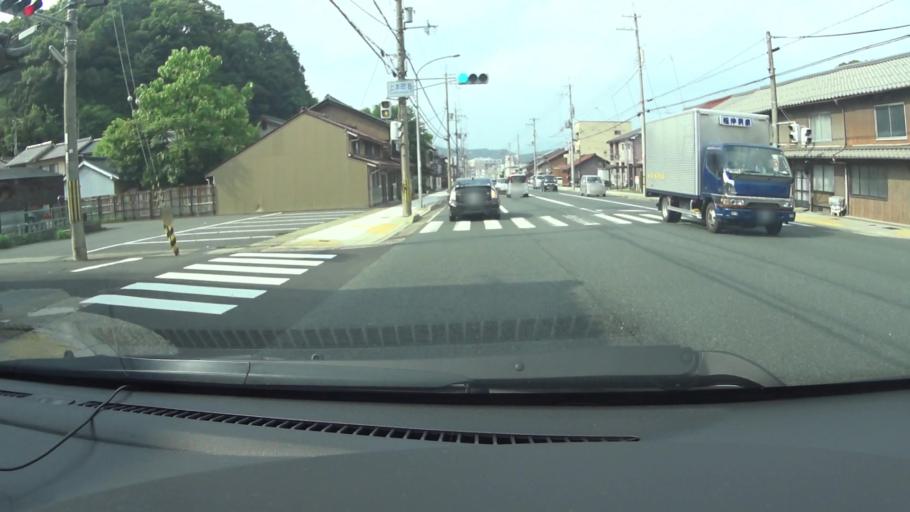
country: JP
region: Kyoto
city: Maizuru
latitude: 35.4689
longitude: 135.3648
